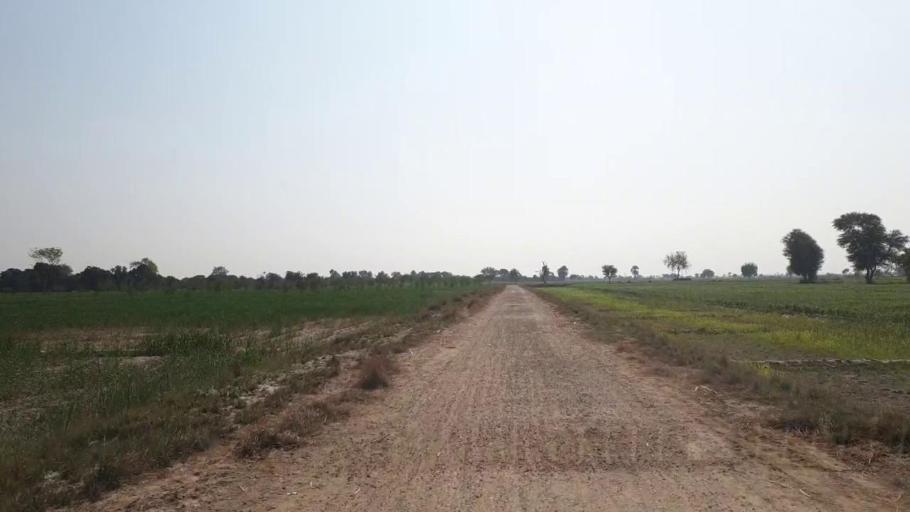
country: PK
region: Sindh
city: Shahdadpur
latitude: 25.9449
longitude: 68.4859
